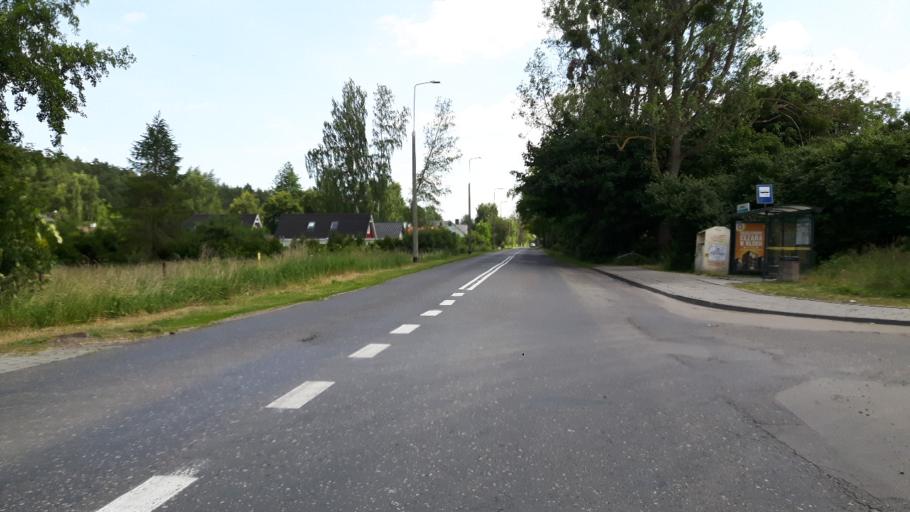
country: PL
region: Pomeranian Voivodeship
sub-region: Powiat gdanski
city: Cedry Wielkie
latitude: 54.3393
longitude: 18.8942
